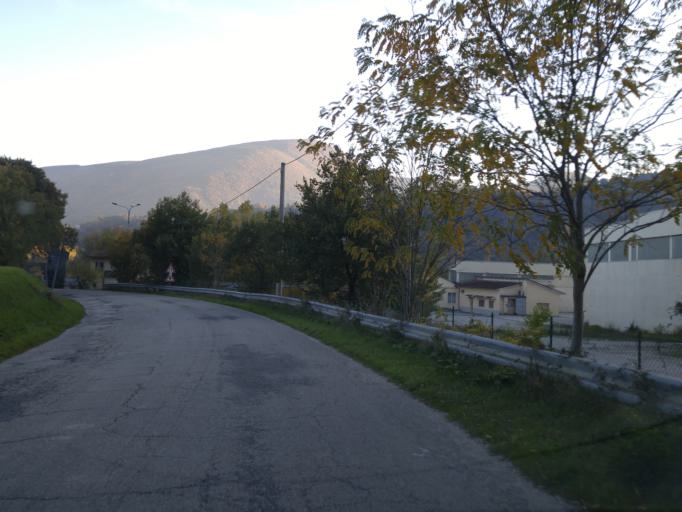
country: IT
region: The Marches
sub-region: Provincia di Pesaro e Urbino
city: Canavaccio
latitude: 43.6772
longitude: 12.7494
